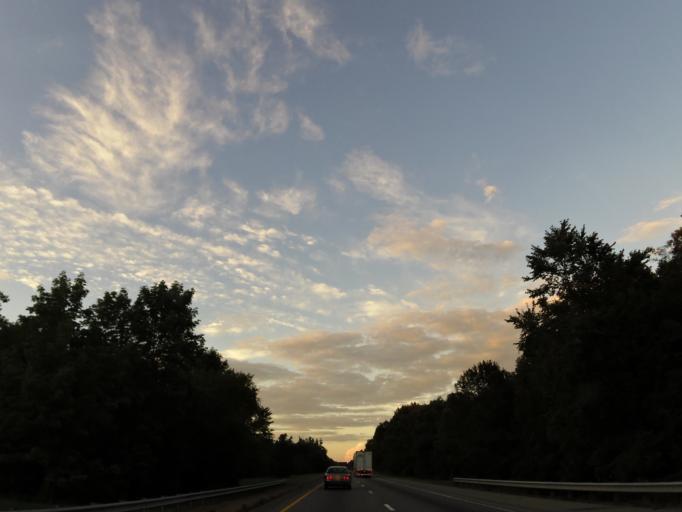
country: US
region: Tennessee
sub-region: Monroe County
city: Sweetwater
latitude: 35.5620
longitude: -84.5513
